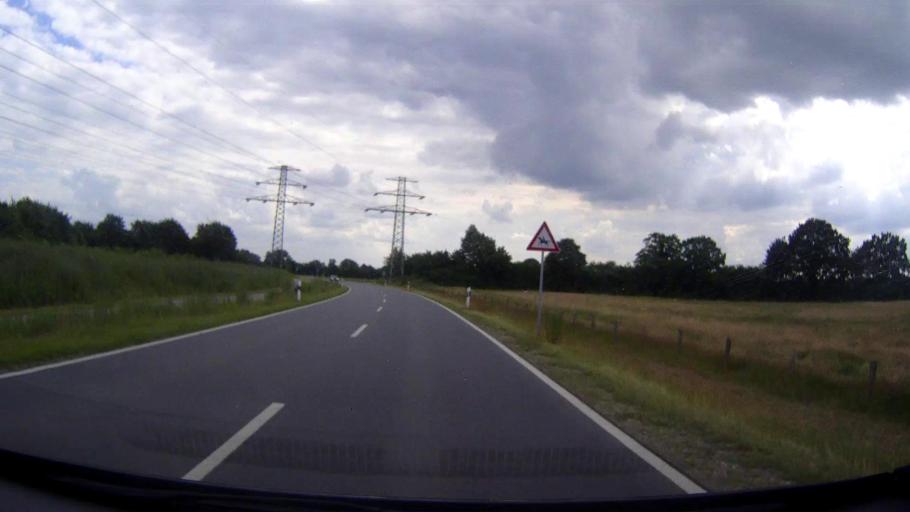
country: DE
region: Schleswig-Holstein
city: Badendorf
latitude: 53.8813
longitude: 10.6031
